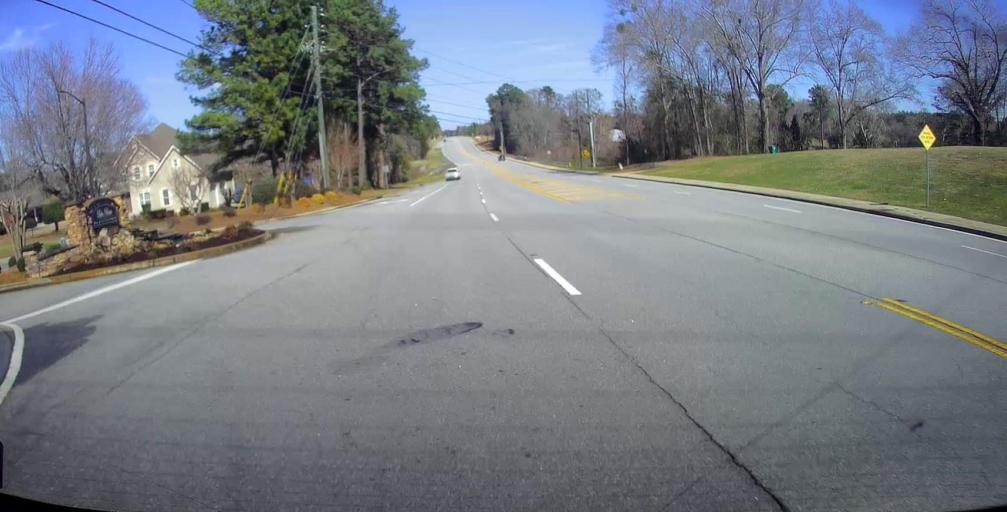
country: US
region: Georgia
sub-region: Houston County
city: Perry
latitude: 32.5167
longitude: -83.6458
